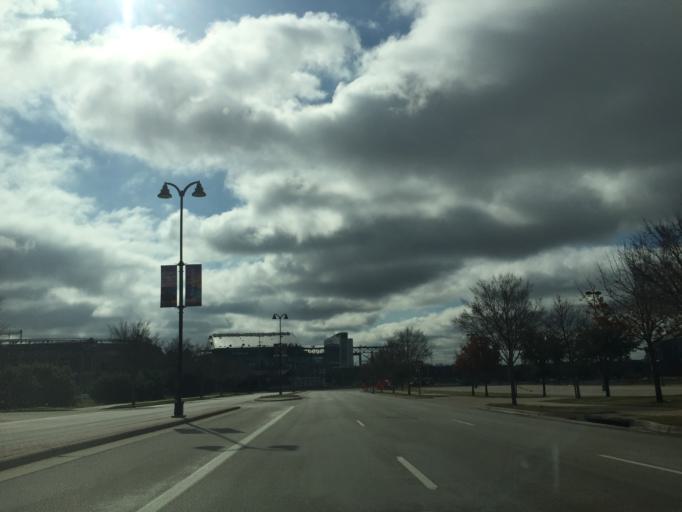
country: US
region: Texas
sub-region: Tarrant County
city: Arlington
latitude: 32.7564
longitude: -97.0854
